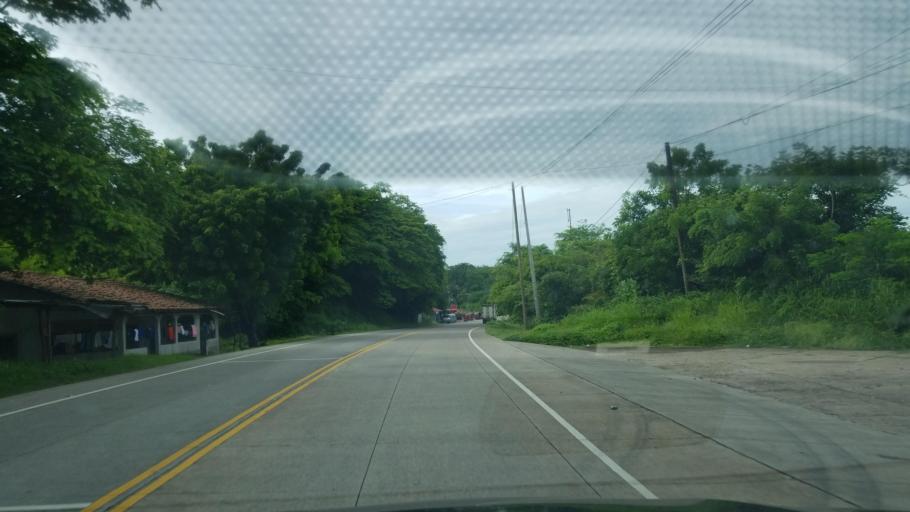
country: HN
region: Choluteca
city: Pespire
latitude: 13.6180
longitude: -87.3702
